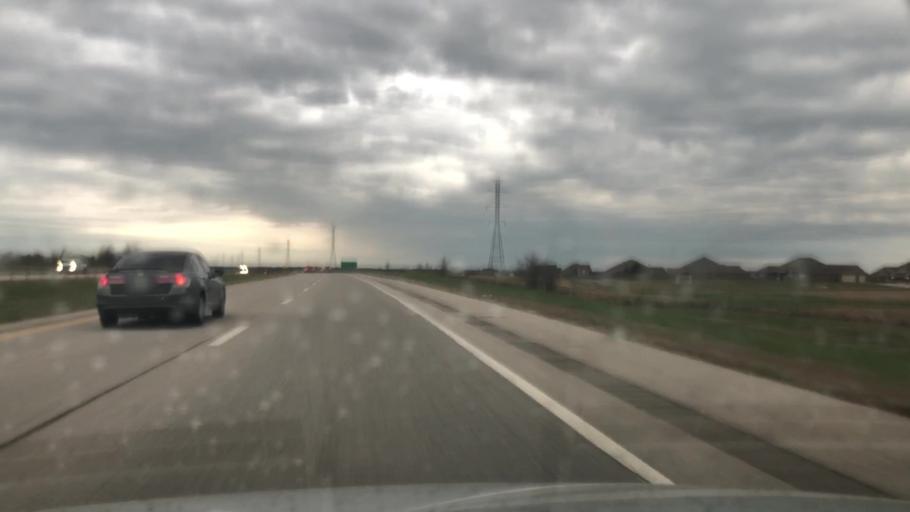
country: US
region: Oklahoma
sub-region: Tulsa County
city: Sperry
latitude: 36.3429
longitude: -95.9235
